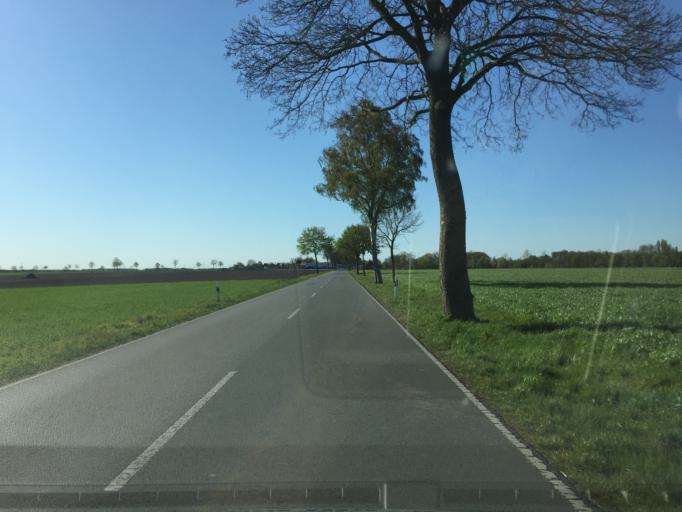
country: DE
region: Lower Saxony
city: Varrel
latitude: 52.6313
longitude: 8.7381
